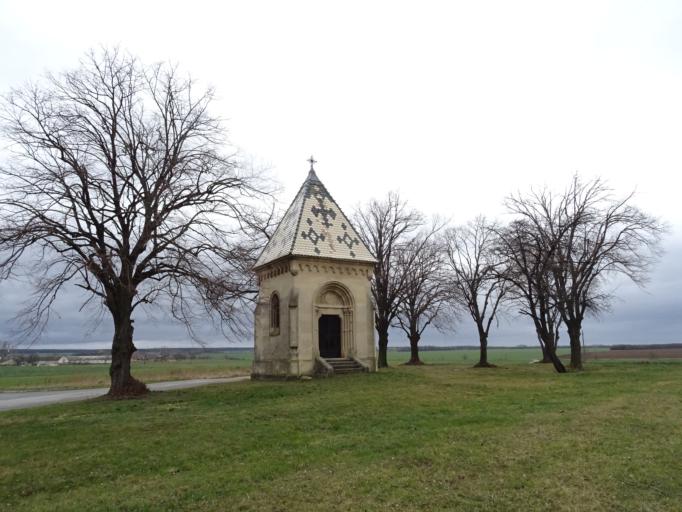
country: AT
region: Burgenland
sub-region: Politischer Bezirk Oberpullendorf
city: Lutzmannsburg
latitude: 47.4609
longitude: 16.6795
